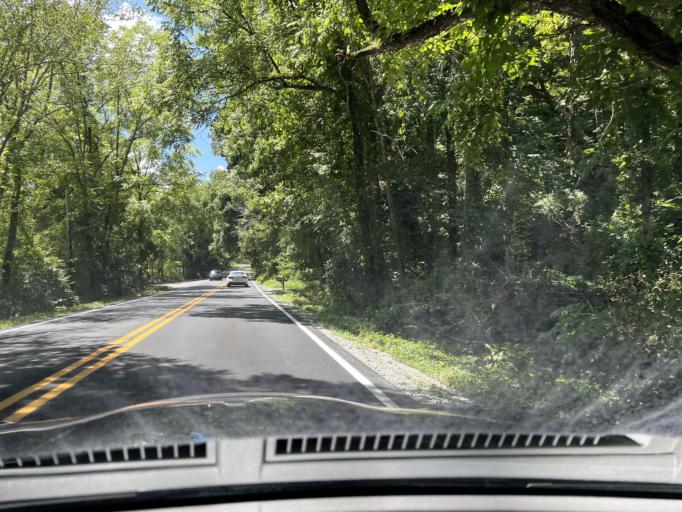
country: US
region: North Carolina
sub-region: Buncombe County
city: Fairview
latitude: 35.4902
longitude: -82.4323
